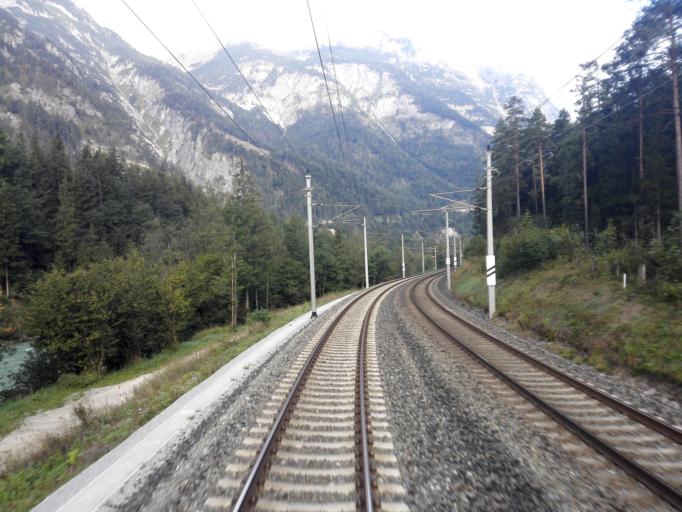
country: AT
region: Salzburg
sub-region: Politischer Bezirk Sankt Johann im Pongau
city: Werfen
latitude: 47.5130
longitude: 13.1685
